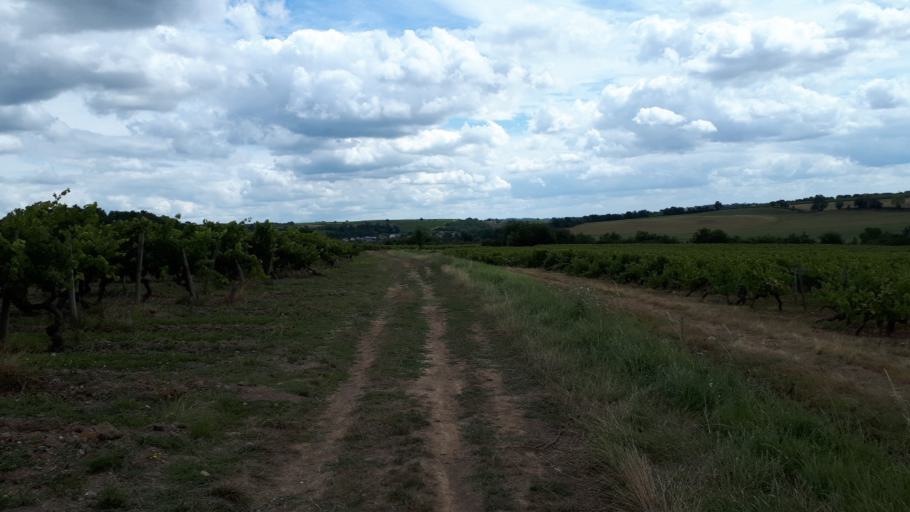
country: FR
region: Pays de la Loire
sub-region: Departement de Maine-et-Loire
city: Rochefort-sur-Loire
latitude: 47.3283
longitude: -0.6819
